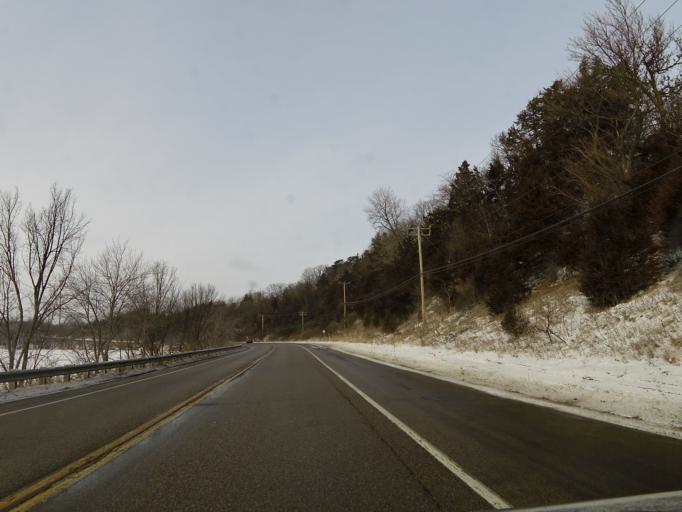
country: US
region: Minnesota
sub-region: Carver County
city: Victoria
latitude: 44.8901
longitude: -93.6599
